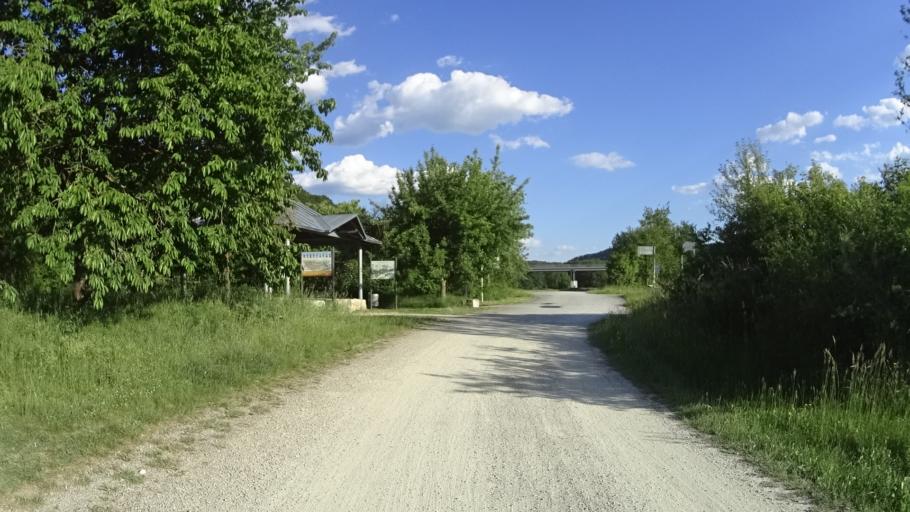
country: DE
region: Bavaria
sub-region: Upper Palatinate
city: Dietfurt
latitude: 48.9954
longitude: 11.6314
